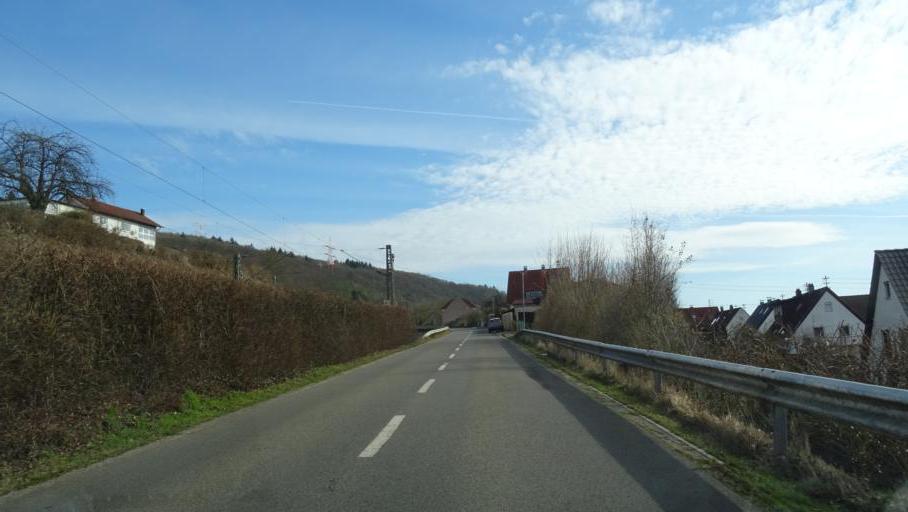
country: DE
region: Baden-Wuerttemberg
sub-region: Karlsruhe Region
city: Neckarzimmern
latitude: 49.3201
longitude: 9.1285
